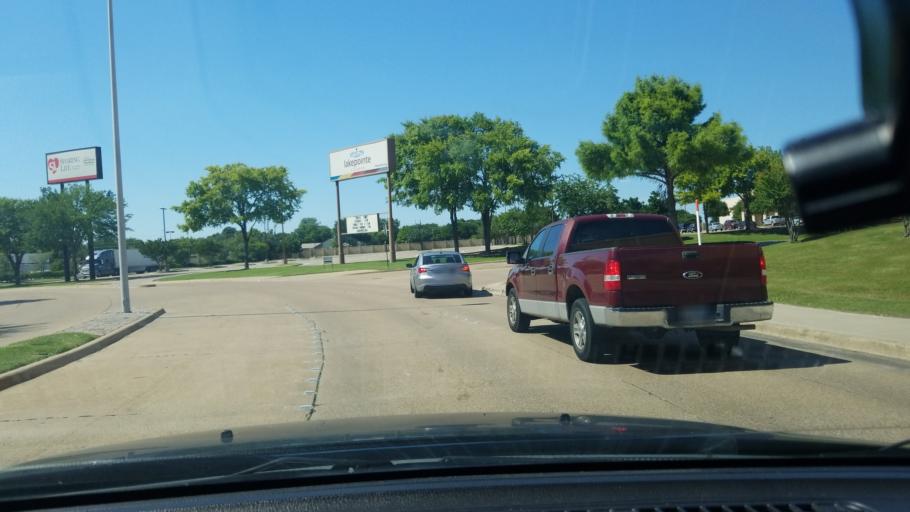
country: US
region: Texas
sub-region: Dallas County
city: Mesquite
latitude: 32.8142
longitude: -96.6223
